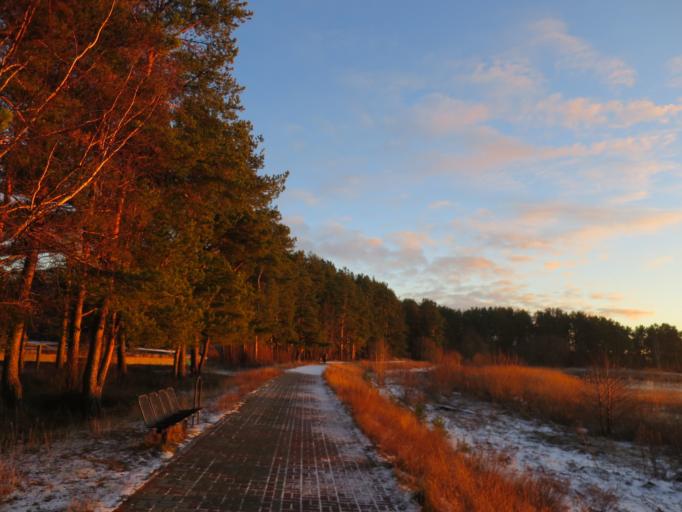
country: LV
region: Riga
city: Bergi
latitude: 56.9772
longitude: 24.3050
